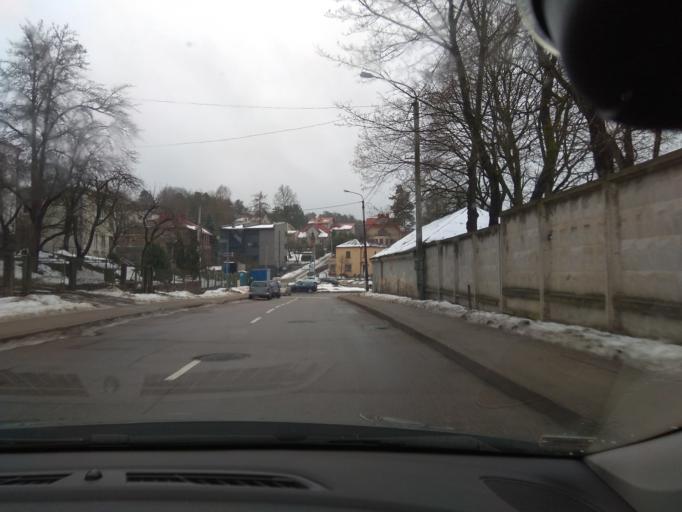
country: LT
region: Vilnius County
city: Rasos
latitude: 54.6985
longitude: 25.3147
